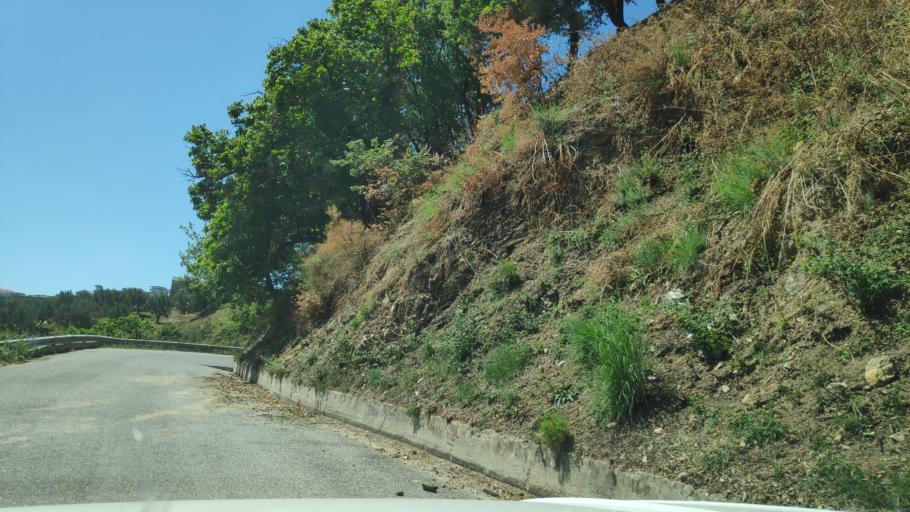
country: IT
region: Calabria
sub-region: Provincia di Catanzaro
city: Montauro
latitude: 38.7459
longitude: 16.5095
